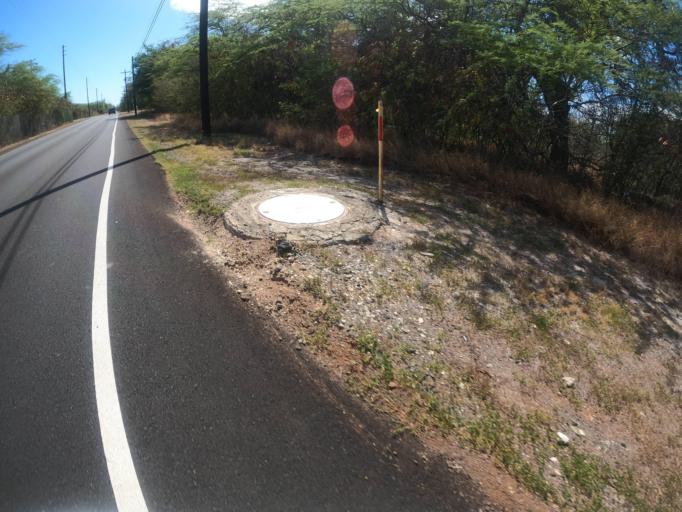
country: US
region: Hawaii
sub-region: Honolulu County
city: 'Ewa Villages
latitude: 21.3104
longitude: -158.0561
